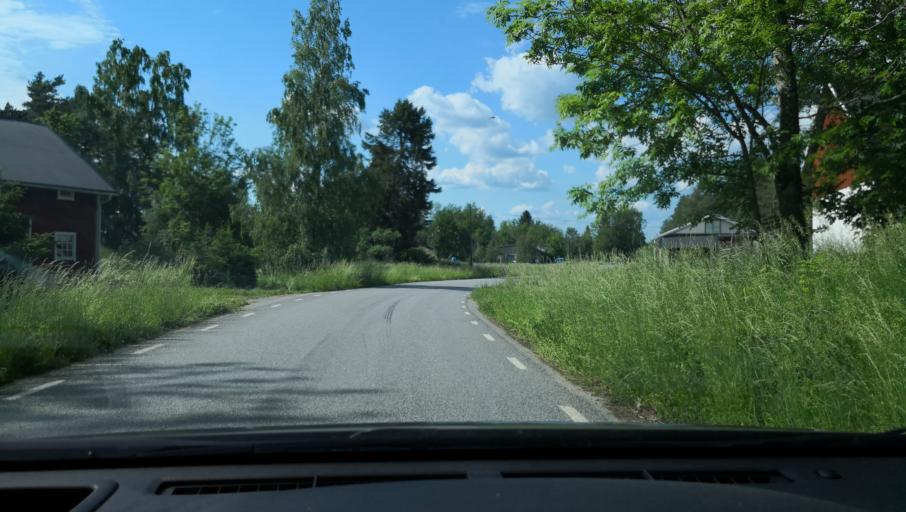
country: SE
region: Uppsala
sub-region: Enkopings Kommun
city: Orsundsbro
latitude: 59.8252
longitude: 17.3200
